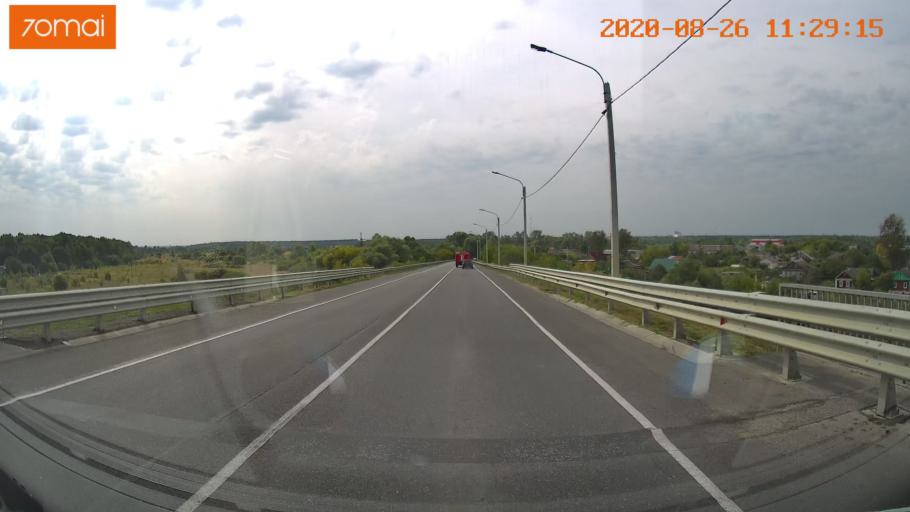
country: RU
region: Rjazan
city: Shilovo
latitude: 54.3214
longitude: 40.9005
